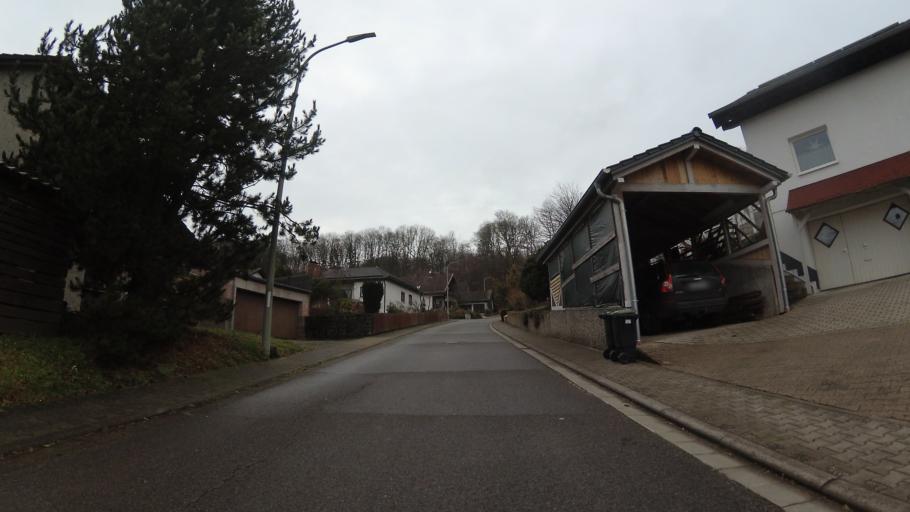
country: DE
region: Rheinland-Pfalz
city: Breitenbach
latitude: 49.4334
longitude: 7.2617
